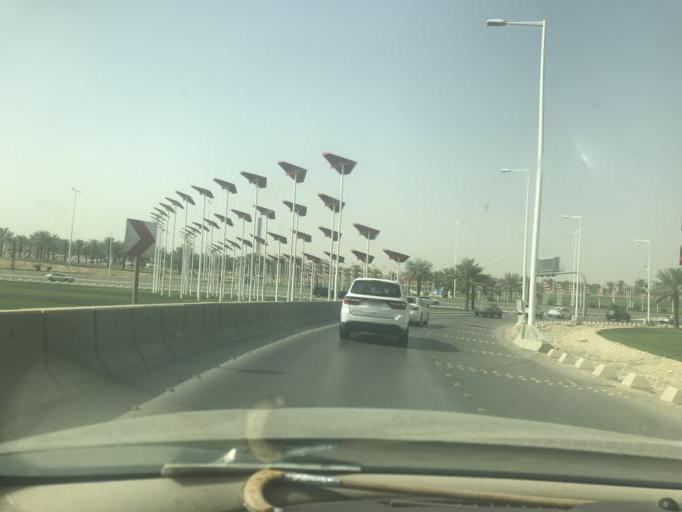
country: SA
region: Ar Riyad
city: Riyadh
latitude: 24.7255
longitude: 46.7083
